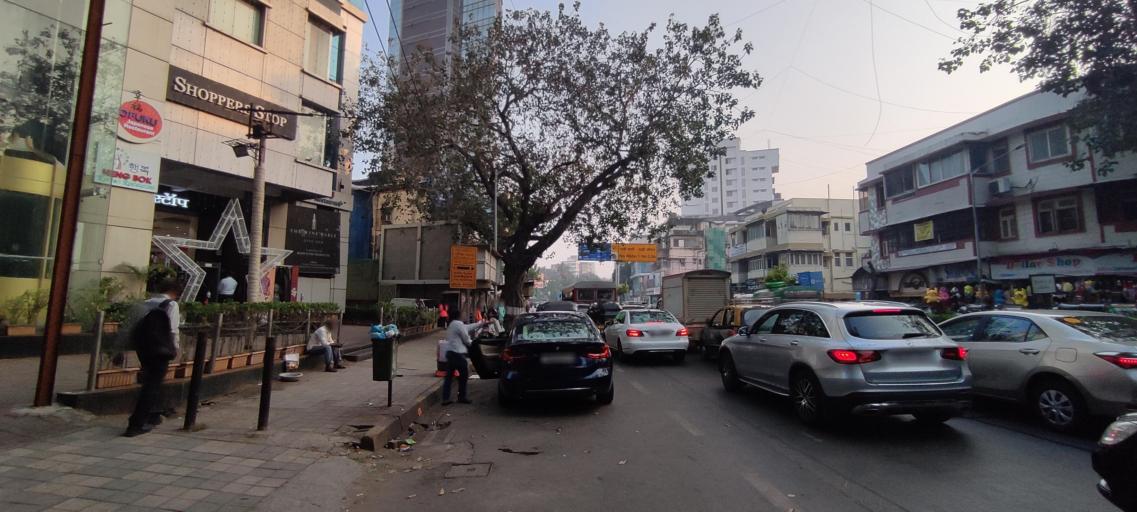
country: IN
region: Maharashtra
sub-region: Mumbai Suburban
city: Mumbai
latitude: 19.0611
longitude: 72.8364
